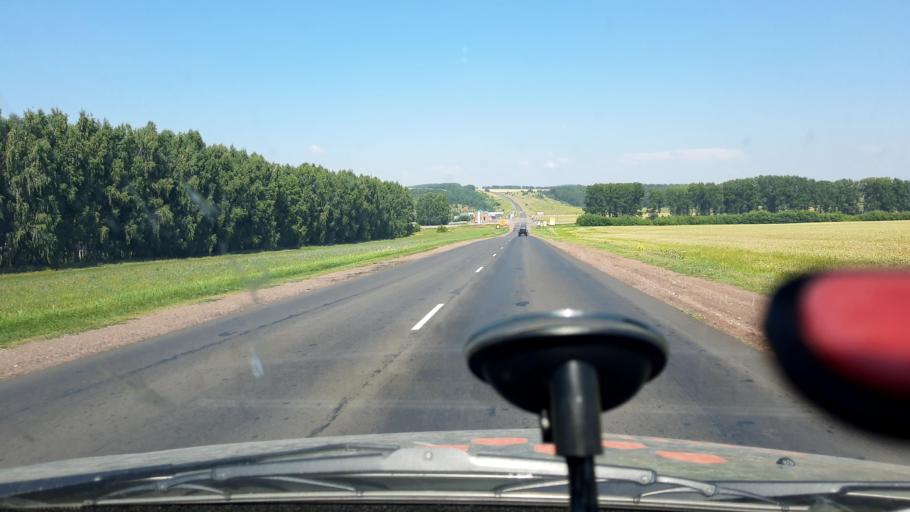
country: RU
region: Bashkortostan
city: Chekmagush
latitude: 55.1271
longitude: 54.6792
